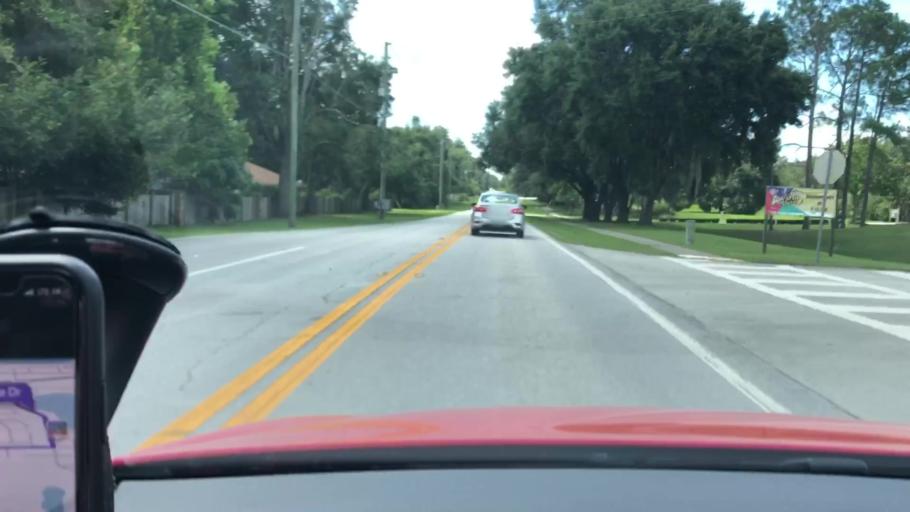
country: US
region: Florida
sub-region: Lake County
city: Eustis
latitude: 28.8461
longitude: -81.6546
